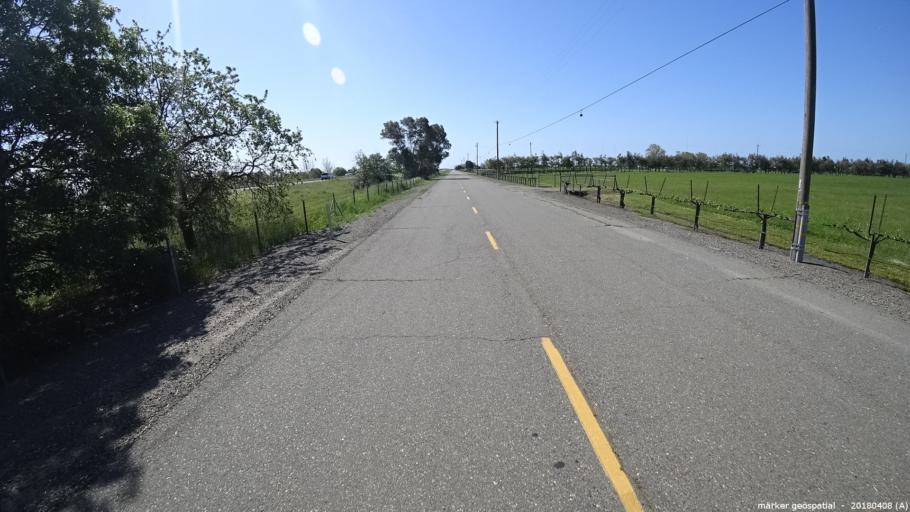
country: US
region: California
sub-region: Sacramento County
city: Laguna
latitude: 38.3348
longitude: -121.4690
